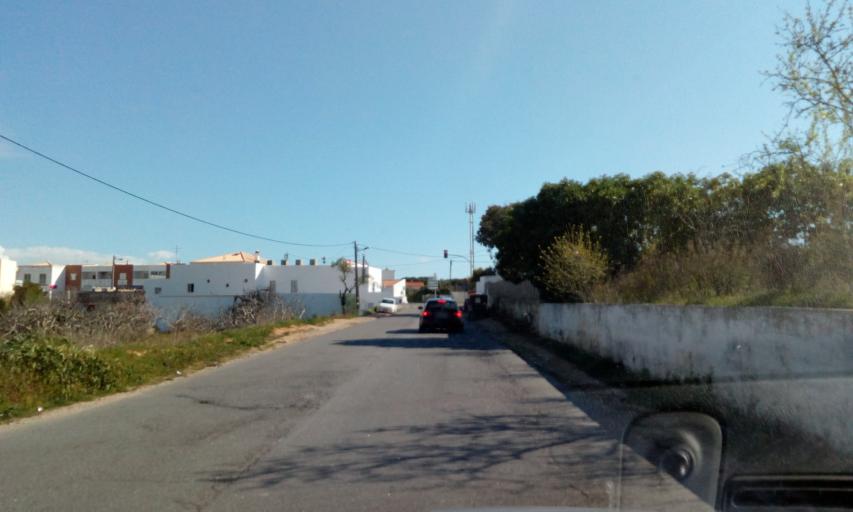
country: PT
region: Faro
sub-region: Albufeira
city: Ferreiras
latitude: 37.1083
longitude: -8.2128
